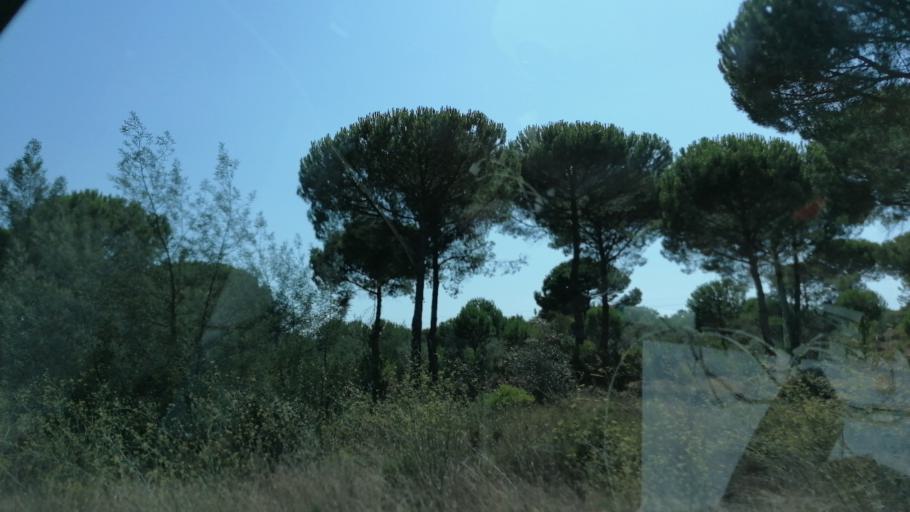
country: PT
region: Evora
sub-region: Vendas Novas
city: Vendas Novas
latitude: 38.7139
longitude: -8.6167
